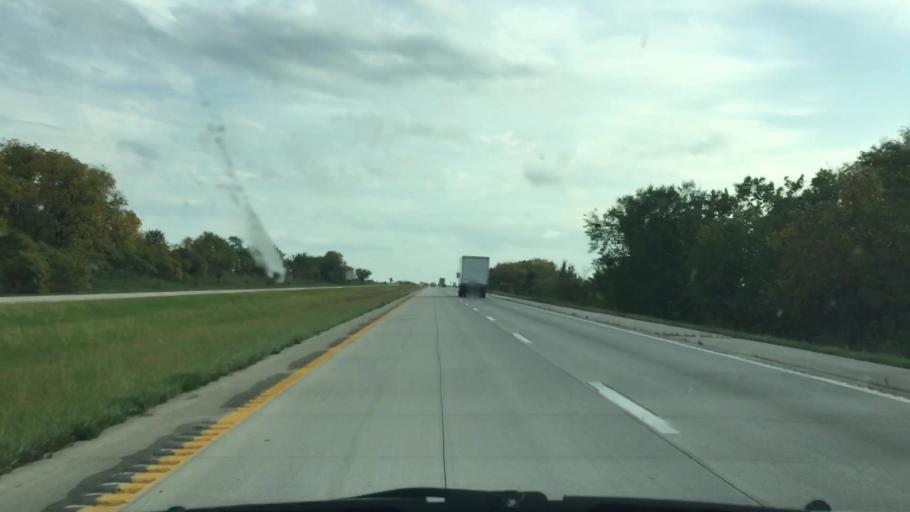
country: US
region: Missouri
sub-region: Daviess County
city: Gallatin
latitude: 39.9821
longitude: -94.0948
